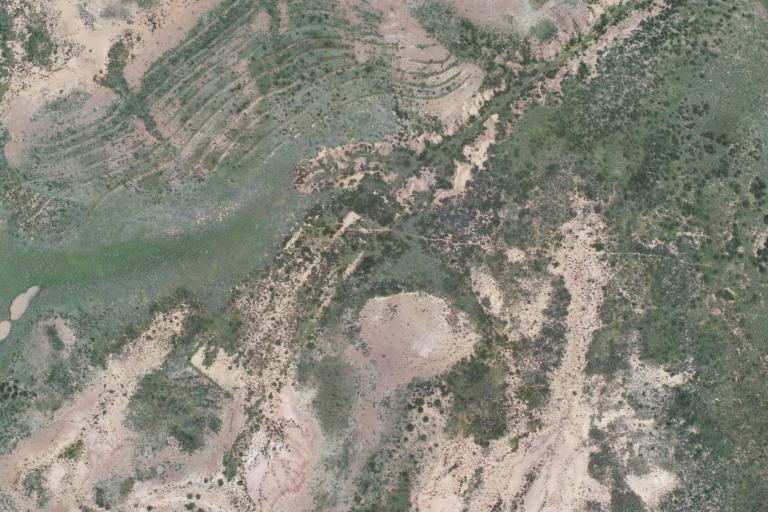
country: BO
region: La Paz
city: Curahuara de Carangas
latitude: -17.2932
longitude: -68.5103
